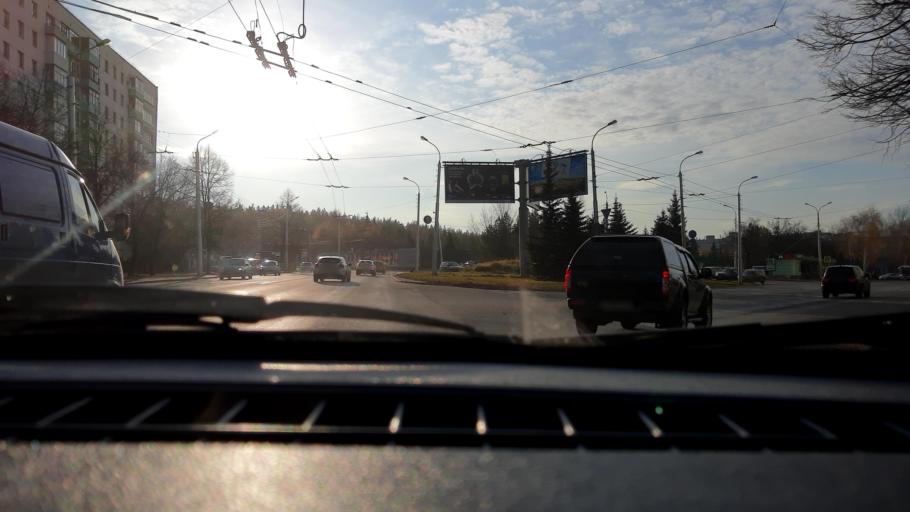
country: RU
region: Bashkortostan
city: Ufa
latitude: 54.7452
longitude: 56.0266
